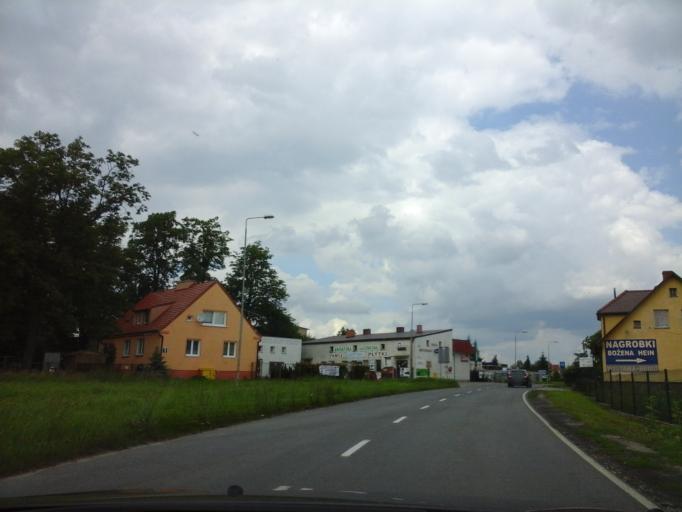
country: PL
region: West Pomeranian Voivodeship
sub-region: Powiat choszczenski
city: Choszczno
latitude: 53.1748
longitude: 15.4167
